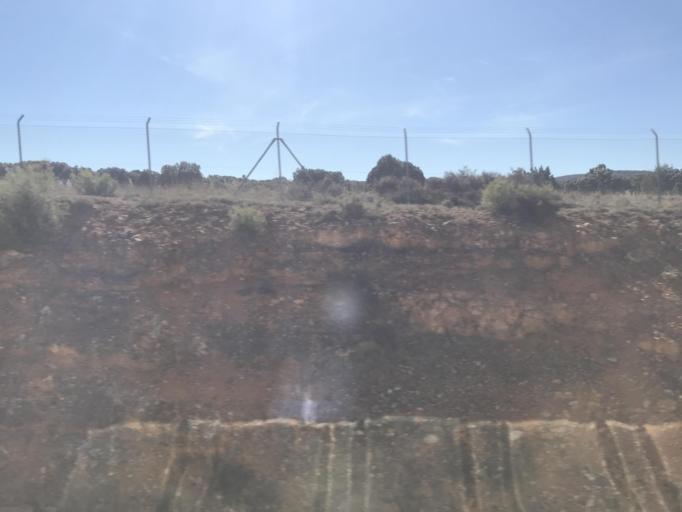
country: ES
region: Castille and Leon
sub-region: Provincia de Soria
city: Arcos de Jalon
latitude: 41.1773
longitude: -2.2309
